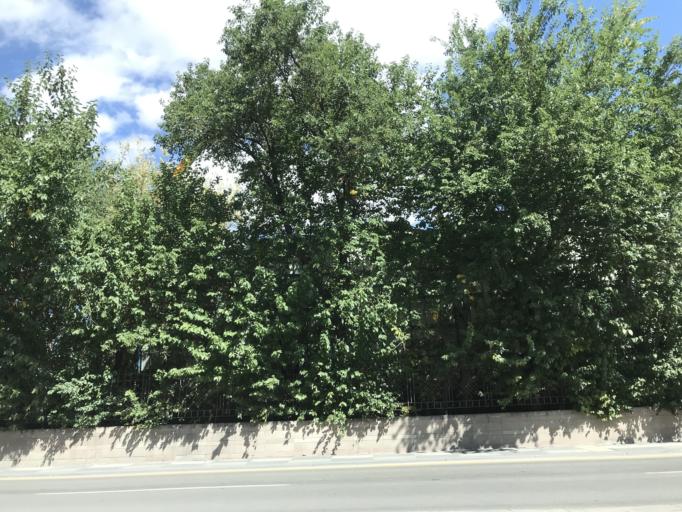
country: TR
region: Ankara
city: Ankara
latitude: 39.9356
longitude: 32.8465
